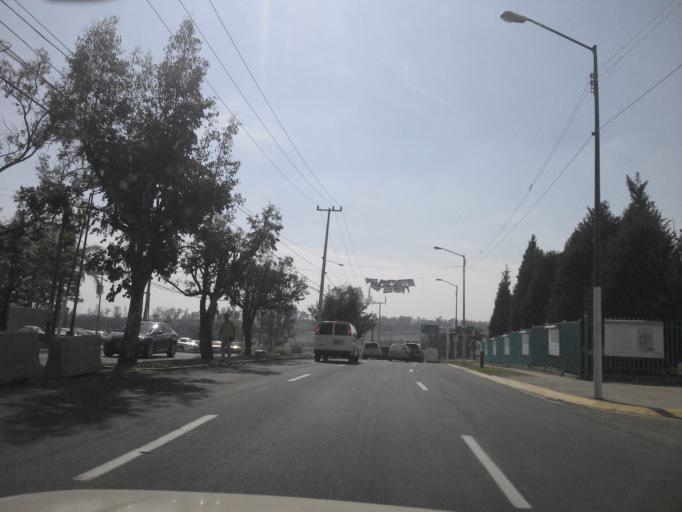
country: MX
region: Jalisco
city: Zapopan2
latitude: 20.7234
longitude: -103.4302
